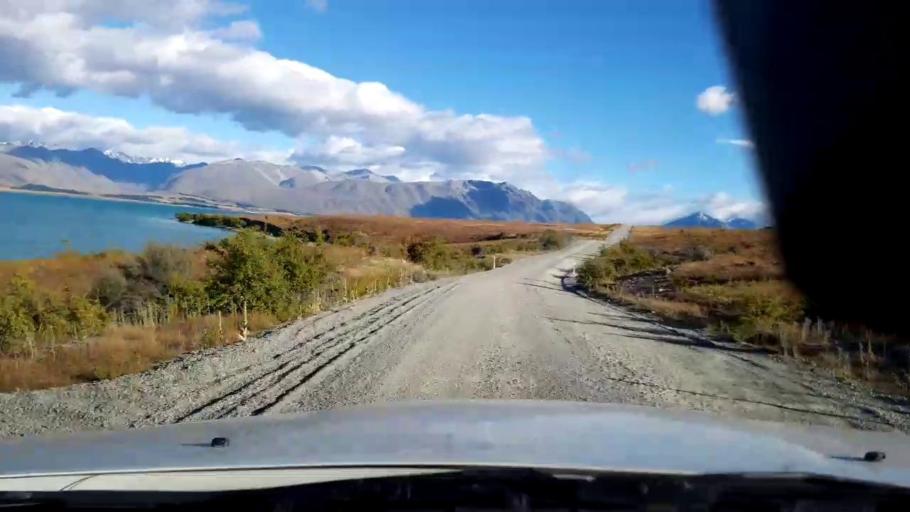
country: NZ
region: Canterbury
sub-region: Timaru District
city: Pleasant Point
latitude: -43.9259
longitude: 170.5604
